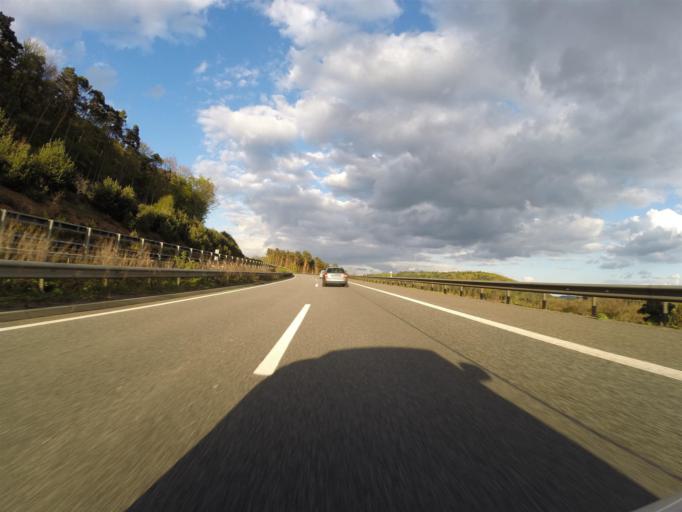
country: DE
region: Rheinland-Pfalz
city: Kaiserslautern
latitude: 49.4617
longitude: 7.8163
